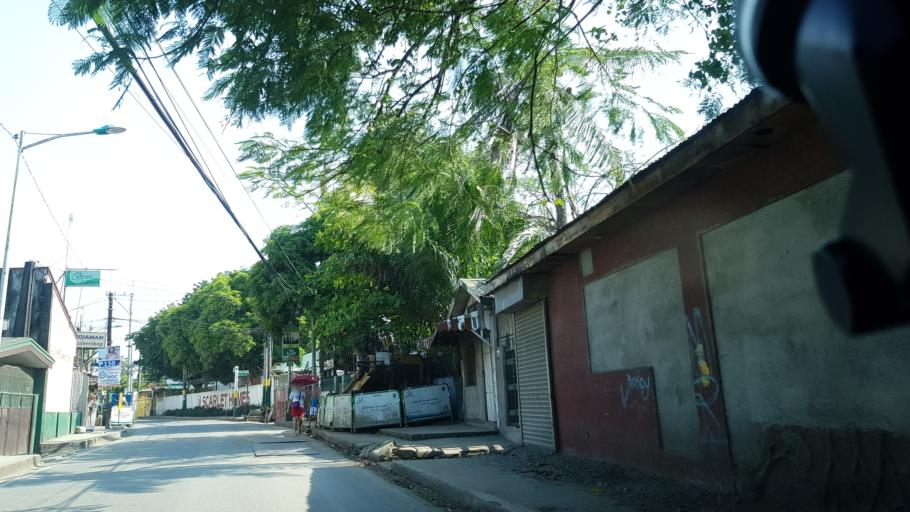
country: PH
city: Sambayanihan People's Village
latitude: 14.4963
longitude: 121.0136
